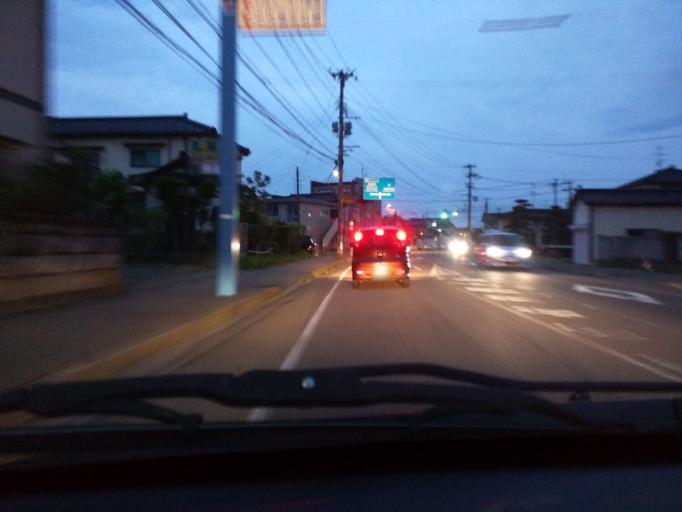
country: JP
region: Niigata
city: Kashiwazaki
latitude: 37.3689
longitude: 138.5738
